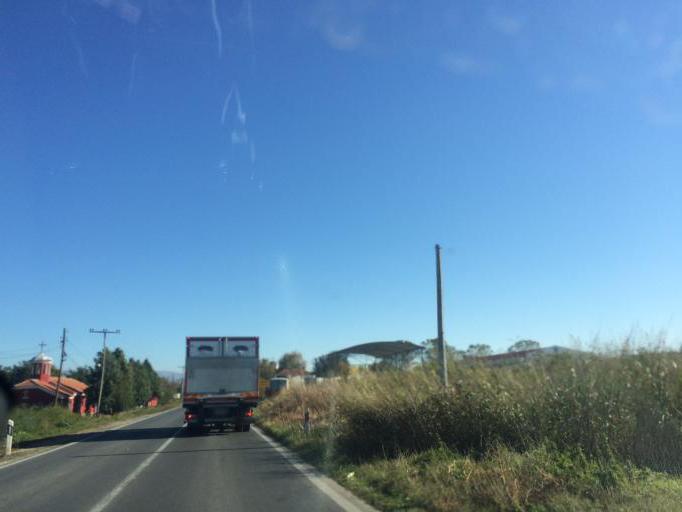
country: MK
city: Obleshevo
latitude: 41.8792
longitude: 22.3273
